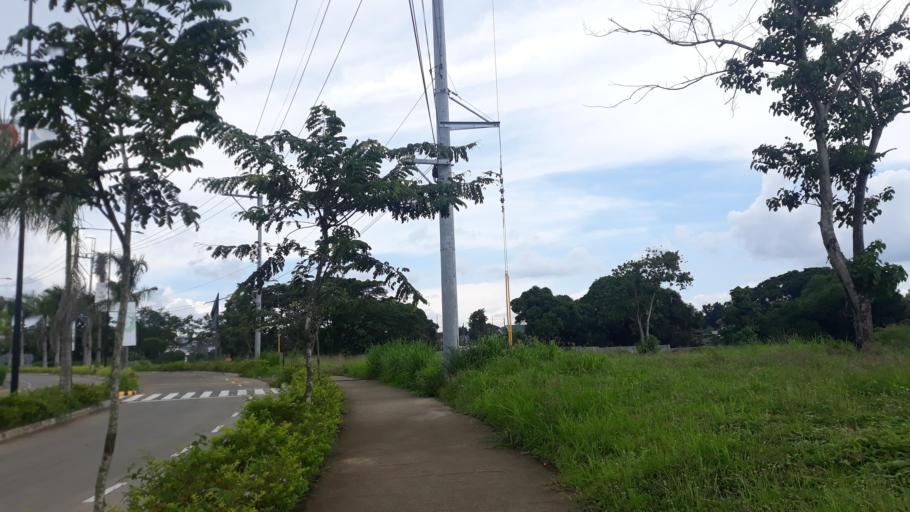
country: PH
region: Calabarzon
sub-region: Province of Cavite
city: Dasmarinas
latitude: 14.3025
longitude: 120.9477
